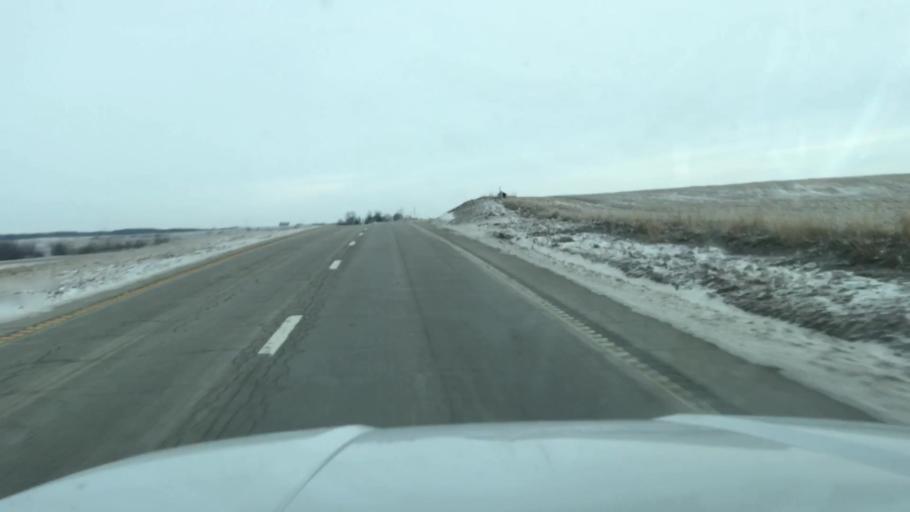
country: US
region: Missouri
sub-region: Andrew County
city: Savannah
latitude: 39.9760
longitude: -94.8760
